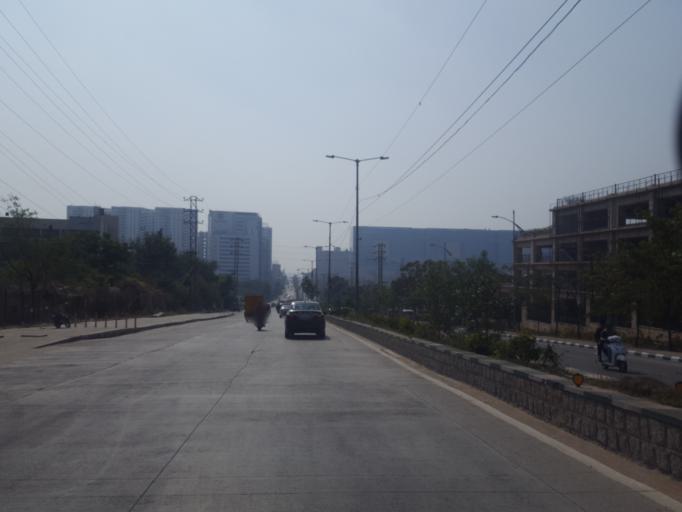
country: IN
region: Telangana
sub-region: Medak
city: Serilingampalle
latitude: 17.4295
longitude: 78.3429
